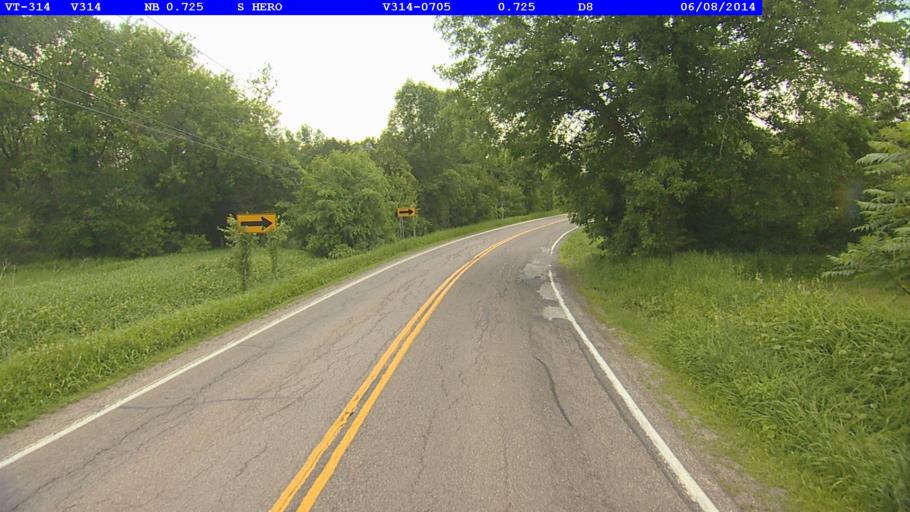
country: US
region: New York
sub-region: Clinton County
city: Cumberland Head
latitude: 44.6689
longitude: -73.3357
